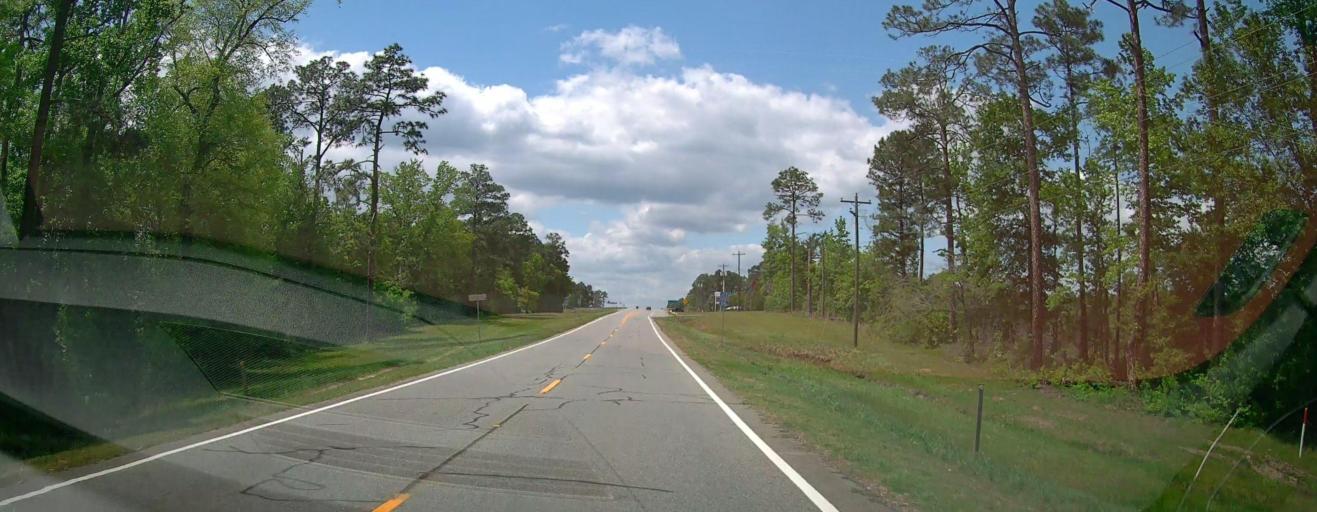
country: US
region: Georgia
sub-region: Treutlen County
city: Soperton
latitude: 32.4351
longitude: -82.6755
